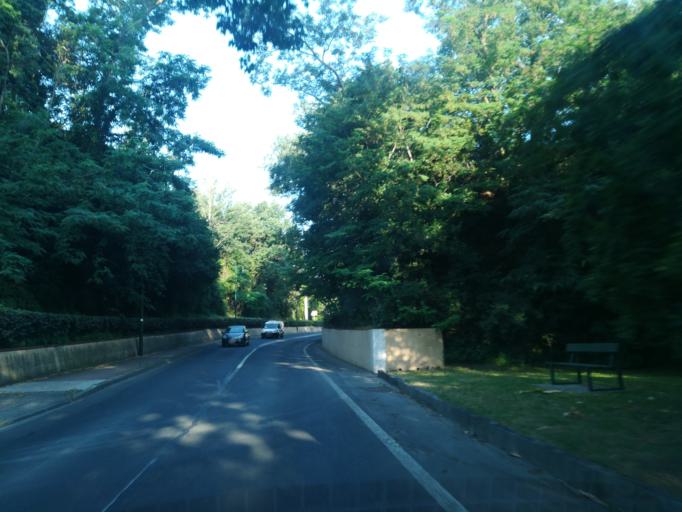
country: FR
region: Languedoc-Roussillon
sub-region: Departement des Pyrenees-Orientales
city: Ceret
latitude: 42.4842
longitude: 2.7566
